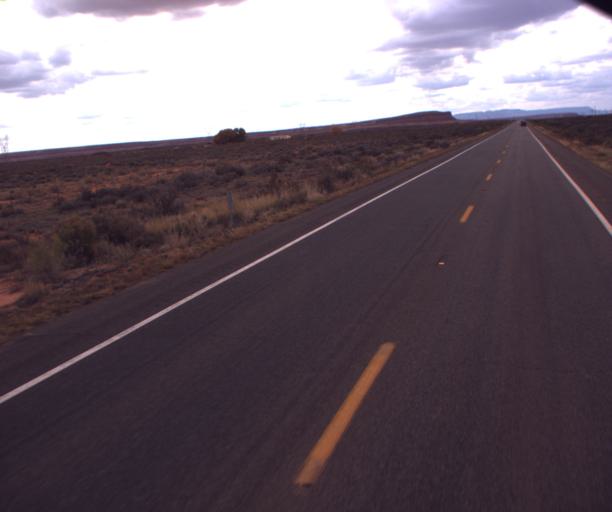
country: US
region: Arizona
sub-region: Navajo County
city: Kayenta
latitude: 36.8182
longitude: -109.8823
